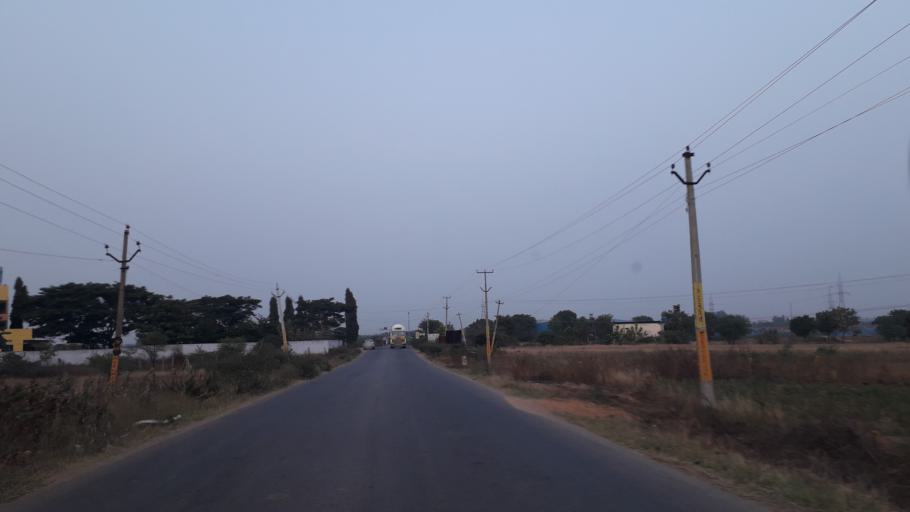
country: IN
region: Telangana
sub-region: Medak
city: Patancheru
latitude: 17.5169
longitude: 78.2327
